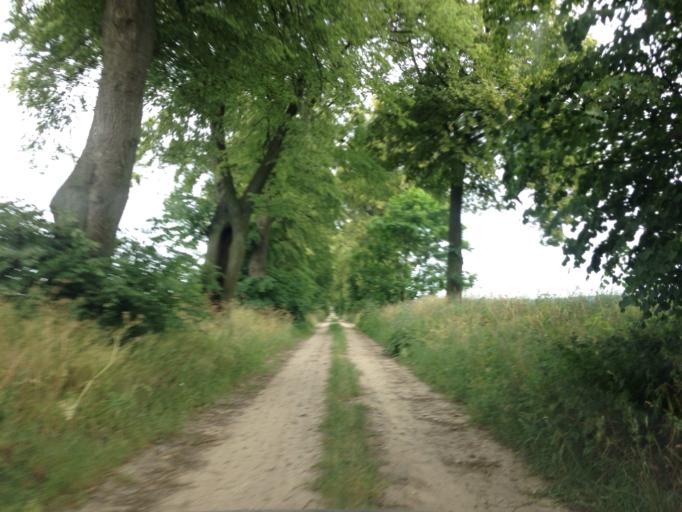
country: PL
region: Kujawsko-Pomorskie
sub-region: Powiat rypinski
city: Wapielsk
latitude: 53.2103
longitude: 19.2498
